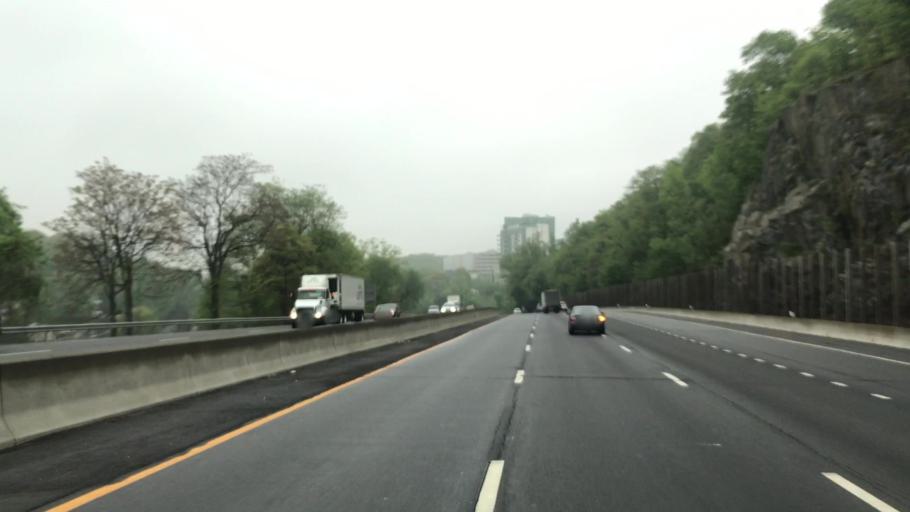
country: US
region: New York
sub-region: Westchester County
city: Tuckahoe
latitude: 40.9583
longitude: -73.8606
